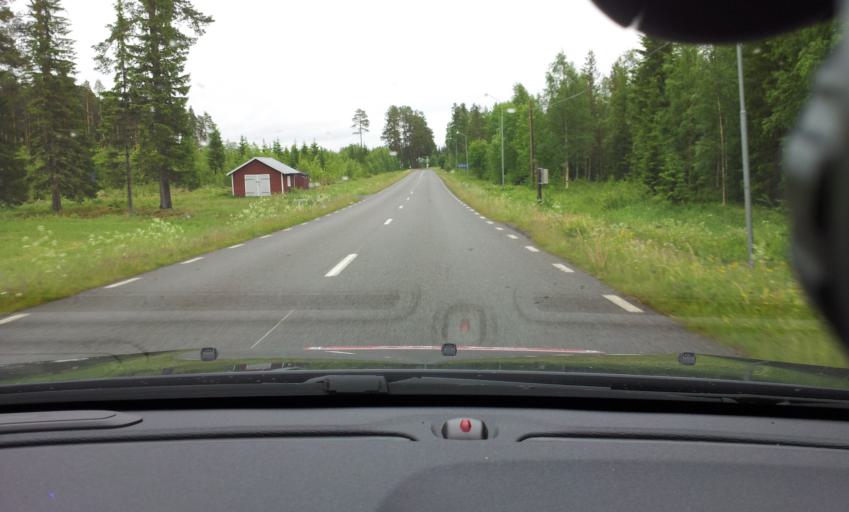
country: SE
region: Jaemtland
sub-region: OEstersunds Kommun
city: Lit
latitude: 63.7177
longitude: 14.9699
